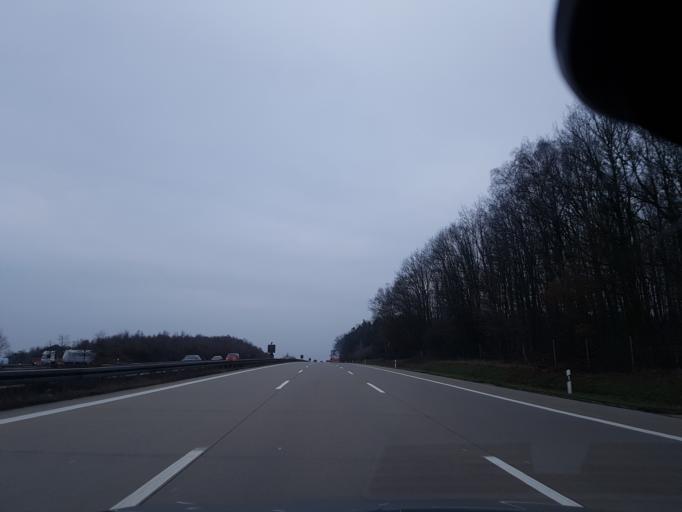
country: DE
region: Saxony
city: Rossau
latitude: 50.9670
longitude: 13.0795
